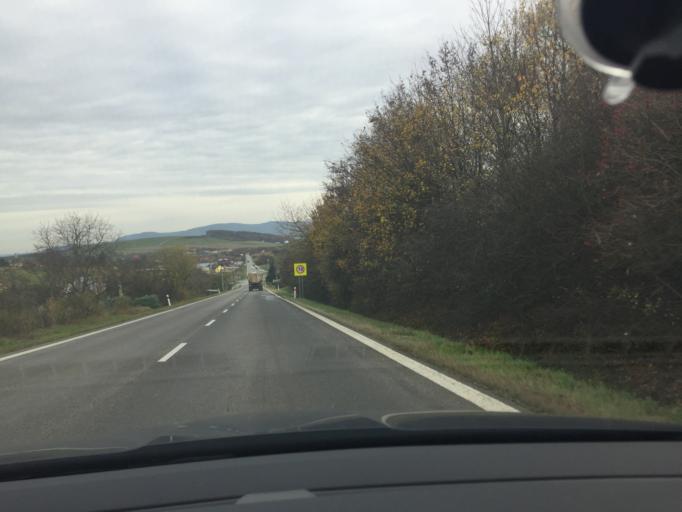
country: SK
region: Presovsky
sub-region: Okres Presov
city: Presov
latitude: 49.0059
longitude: 21.1628
